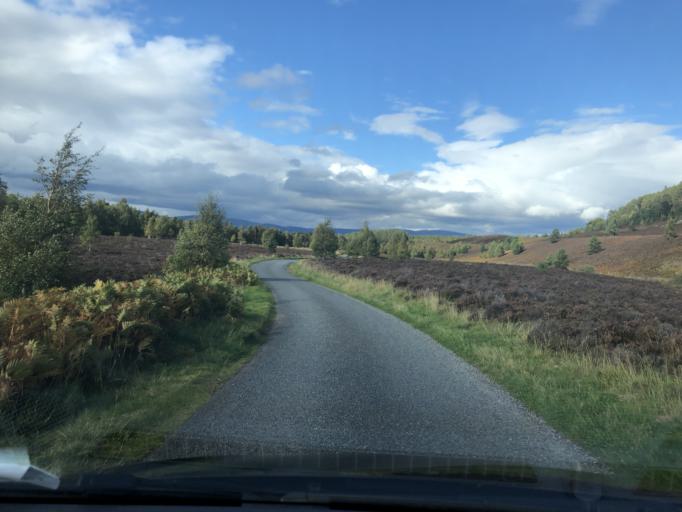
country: GB
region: Scotland
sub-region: Highland
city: Aviemore
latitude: 57.0592
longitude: -3.8949
